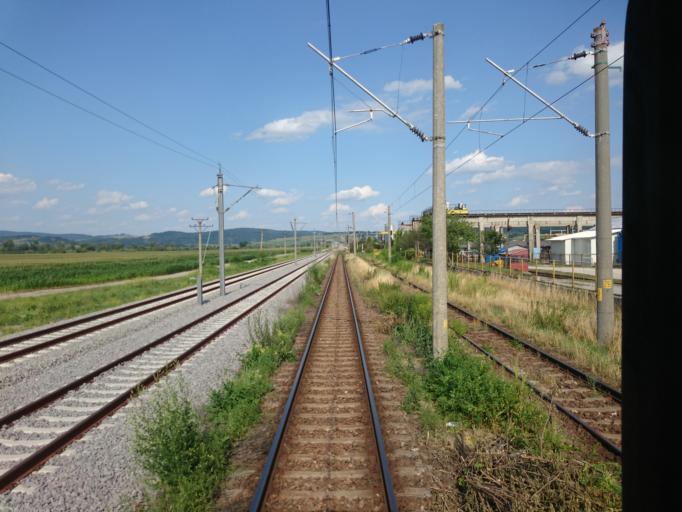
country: RO
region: Mures
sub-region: Comuna Danes
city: Danes
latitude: 46.2255
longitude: 24.7070
